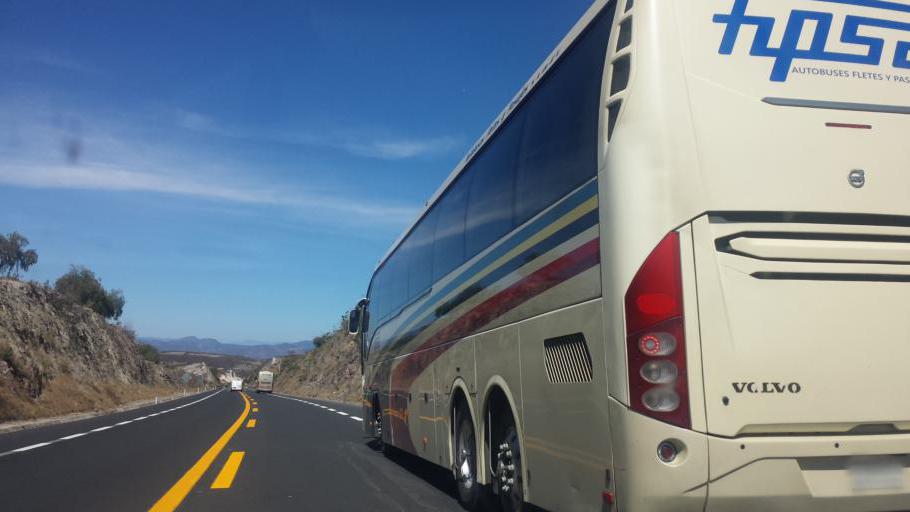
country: MX
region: Oaxaca
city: San Gabriel Casa Blanca
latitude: 17.9515
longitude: -97.3549
